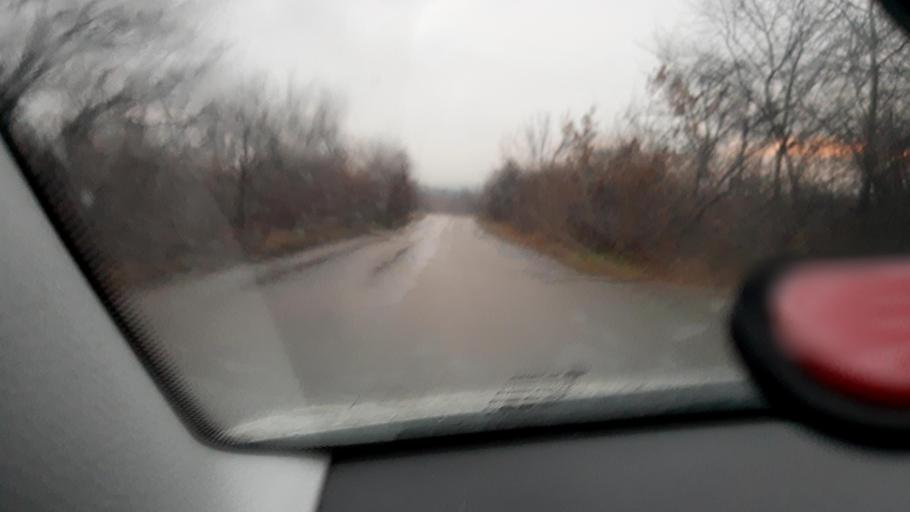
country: RU
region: Bashkortostan
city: Ufa
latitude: 54.8725
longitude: 56.1317
